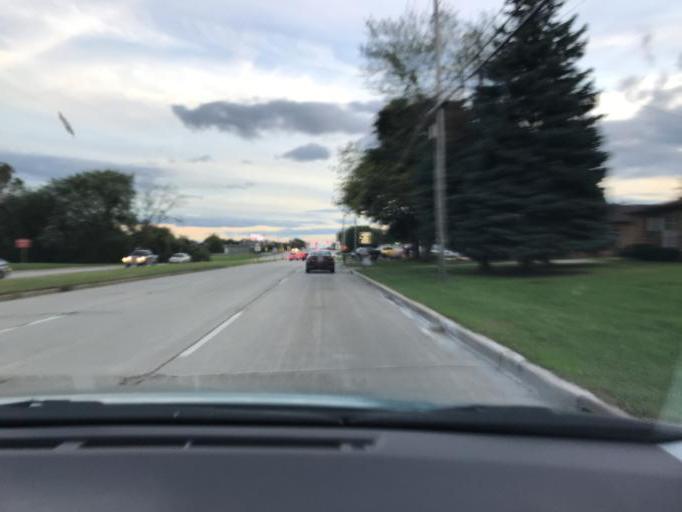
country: US
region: Wisconsin
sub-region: Kenosha County
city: Pleasant Prairie
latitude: 42.5852
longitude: -87.8833
